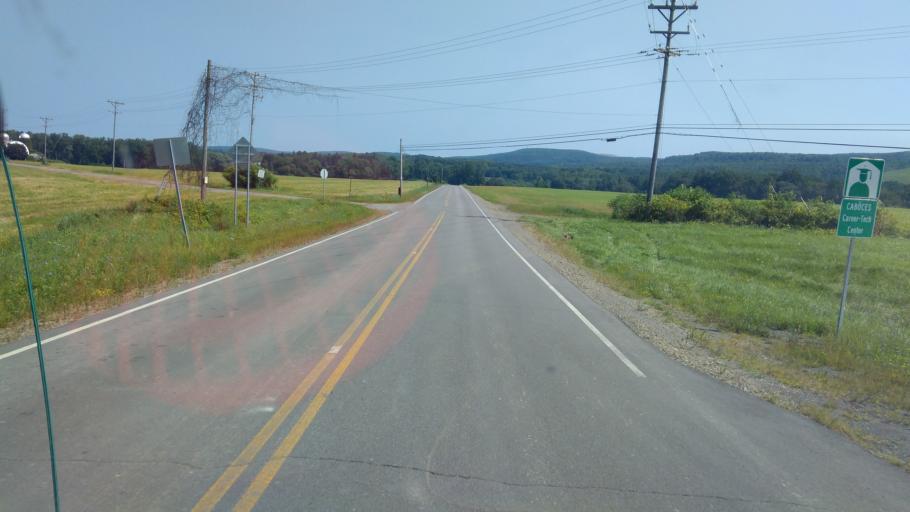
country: US
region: New York
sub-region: Allegany County
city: Belmont
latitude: 42.2556
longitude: -78.0583
